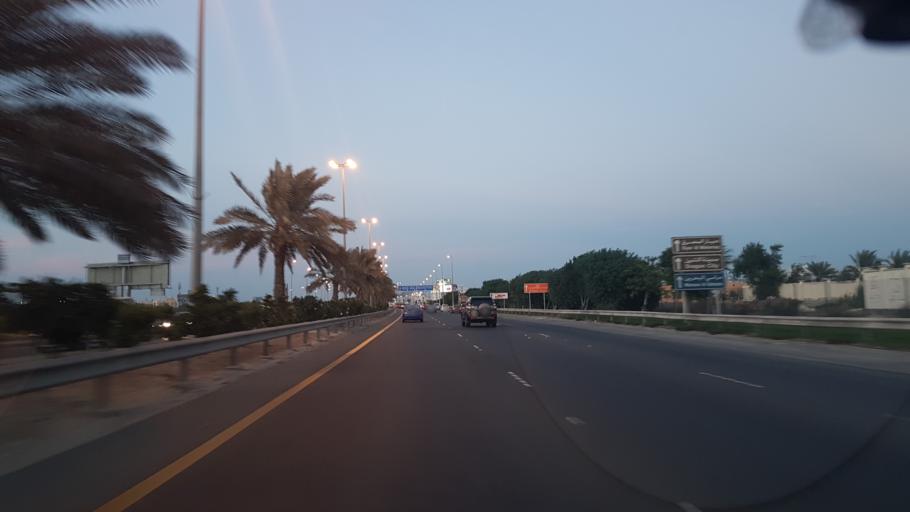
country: BH
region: Manama
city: Jidd Hafs
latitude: 26.2088
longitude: 50.5173
